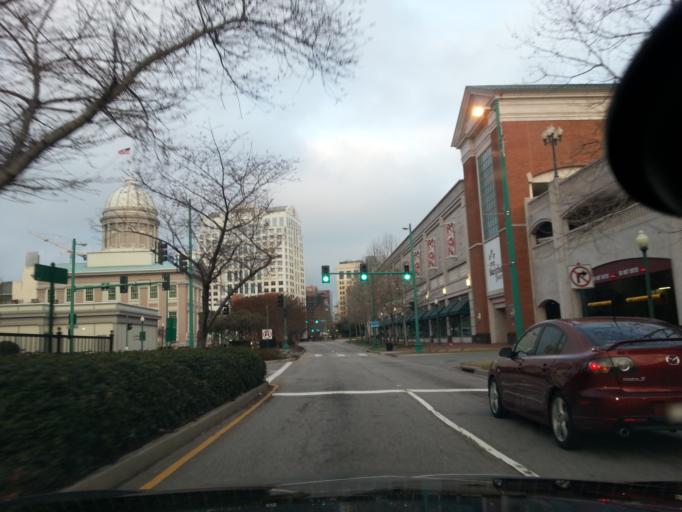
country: US
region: Virginia
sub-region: City of Norfolk
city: Norfolk
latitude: 36.8476
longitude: -76.2874
